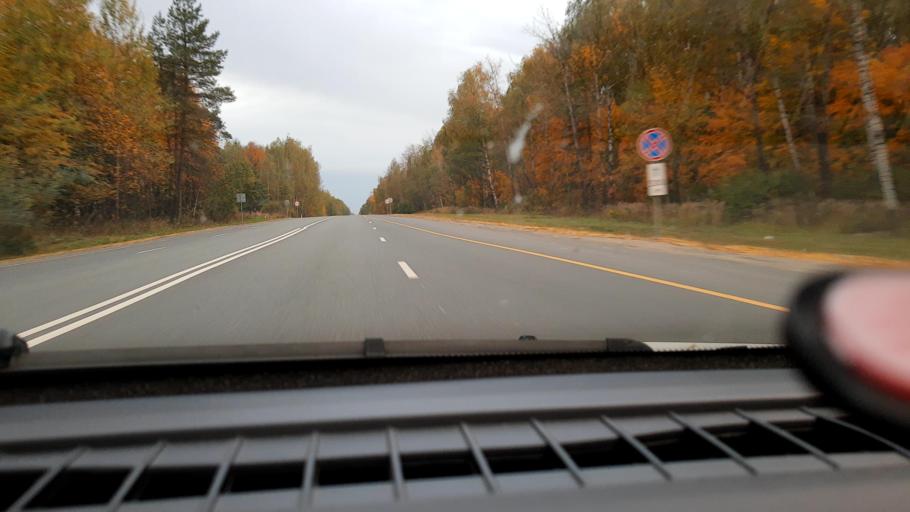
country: RU
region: Vladimir
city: Orgtrud
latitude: 56.2009
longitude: 40.7983
